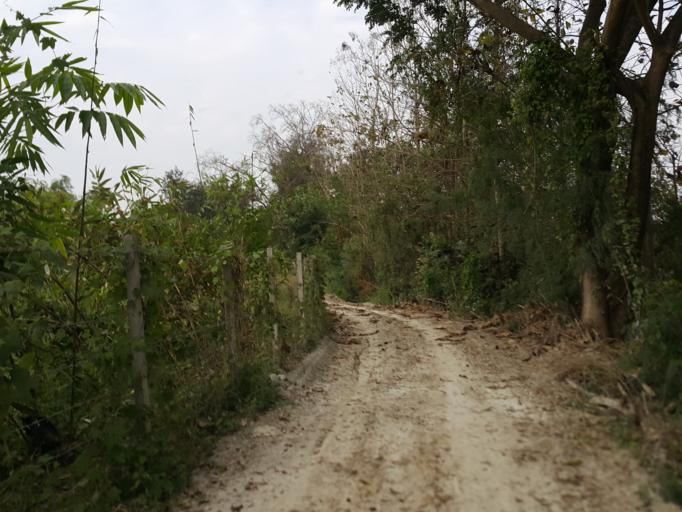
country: TH
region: Chiang Mai
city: San Kamphaeng
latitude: 18.7950
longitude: 99.1160
